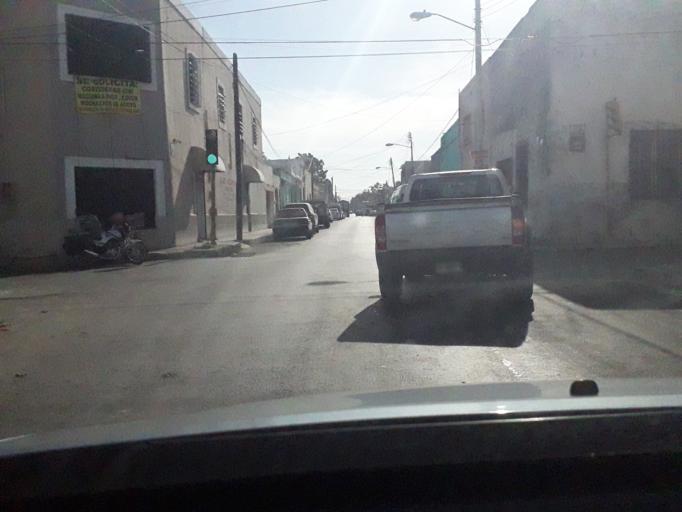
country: MX
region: Yucatan
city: Merida
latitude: 20.9614
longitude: -89.6153
